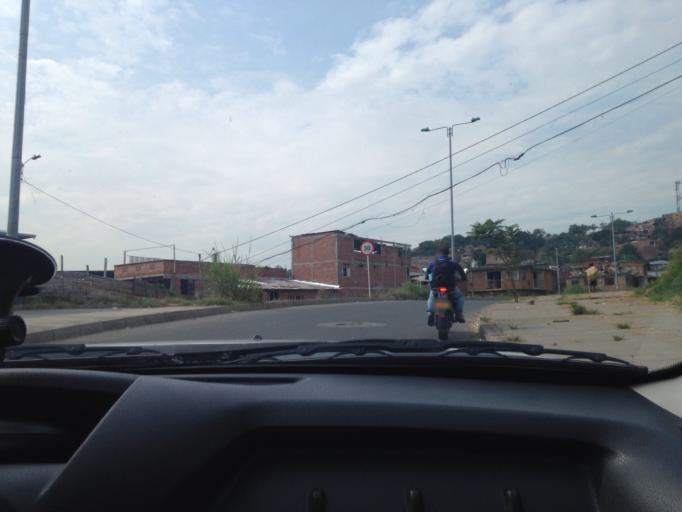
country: CO
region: Valle del Cauca
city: Cali
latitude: 3.3886
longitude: -76.5560
